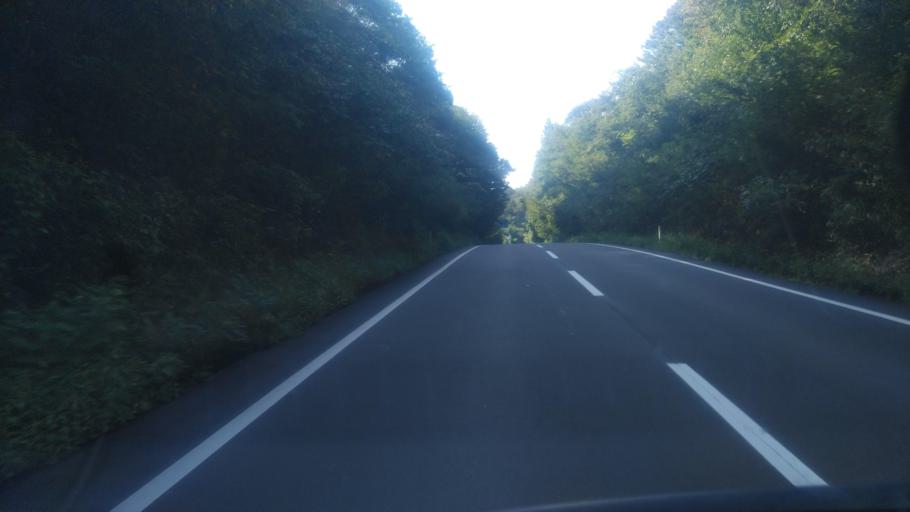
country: JP
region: Miyagi
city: Okawara
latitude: 38.0904
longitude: 140.7132
